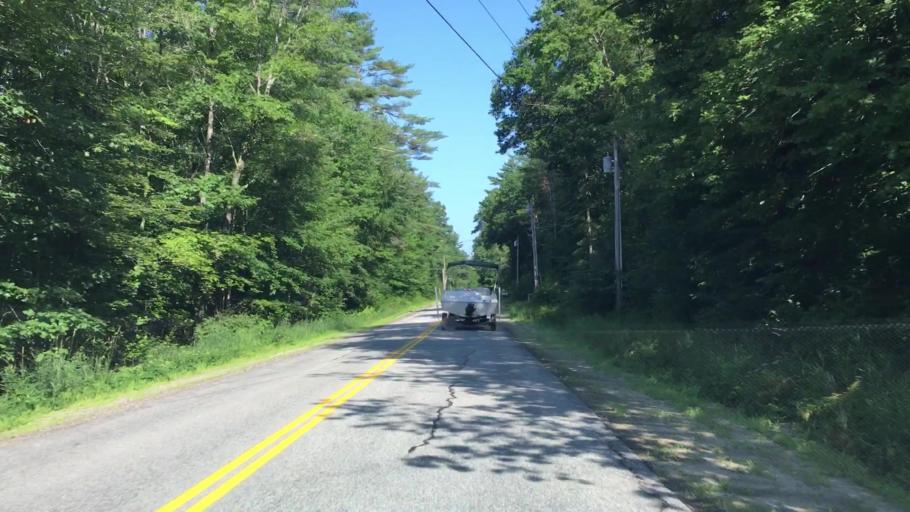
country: US
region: Maine
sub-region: Androscoggin County
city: Poland
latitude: 44.0519
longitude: -70.3722
